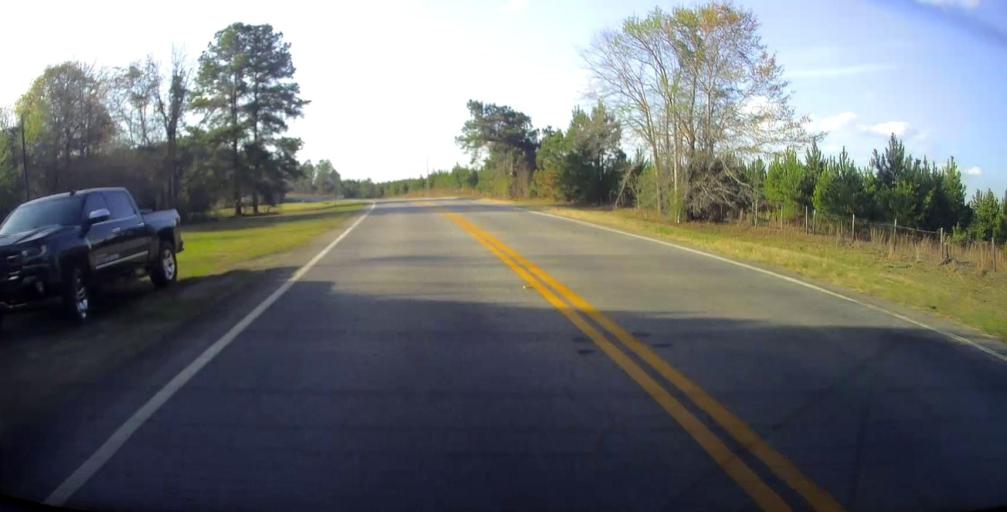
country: US
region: Georgia
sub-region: Toombs County
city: Lyons
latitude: 32.1721
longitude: -82.2760
